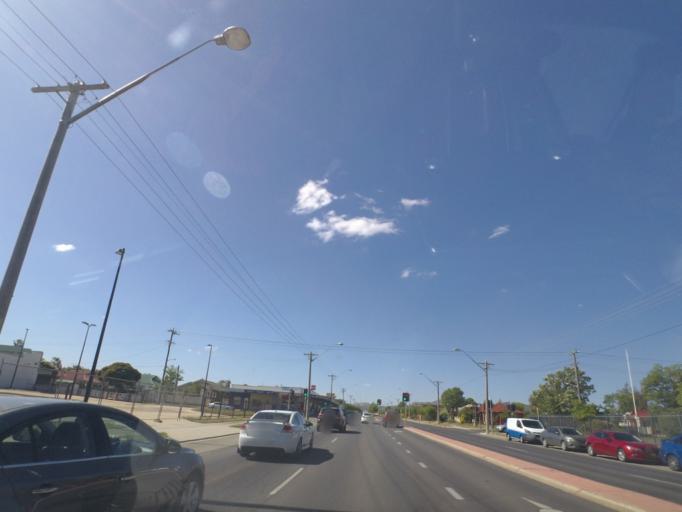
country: AU
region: New South Wales
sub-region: Albury Municipality
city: North Albury
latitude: -36.0635
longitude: 146.9314
